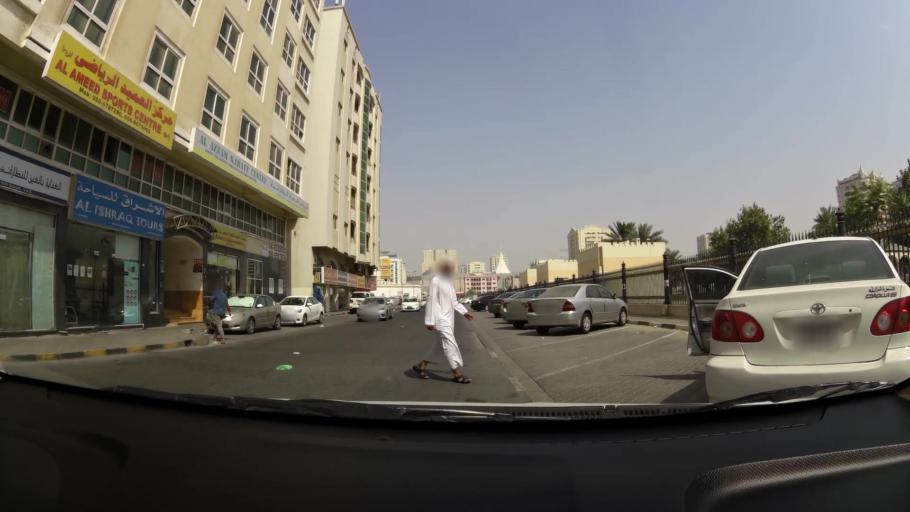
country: AE
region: Ash Shariqah
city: Sharjah
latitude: 25.3479
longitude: 55.3945
